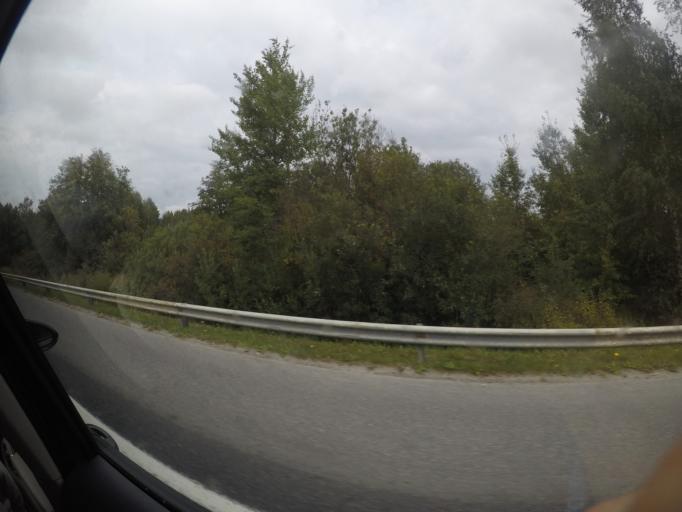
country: FI
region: Haeme
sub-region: Haemeenlinna
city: Parola
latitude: 61.0408
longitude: 24.4023
